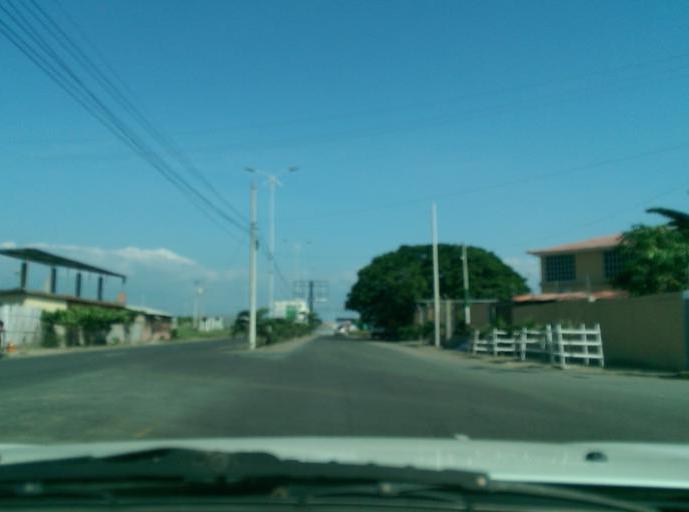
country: EC
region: Manabi
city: Manta
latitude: -0.9581
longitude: -80.6836
